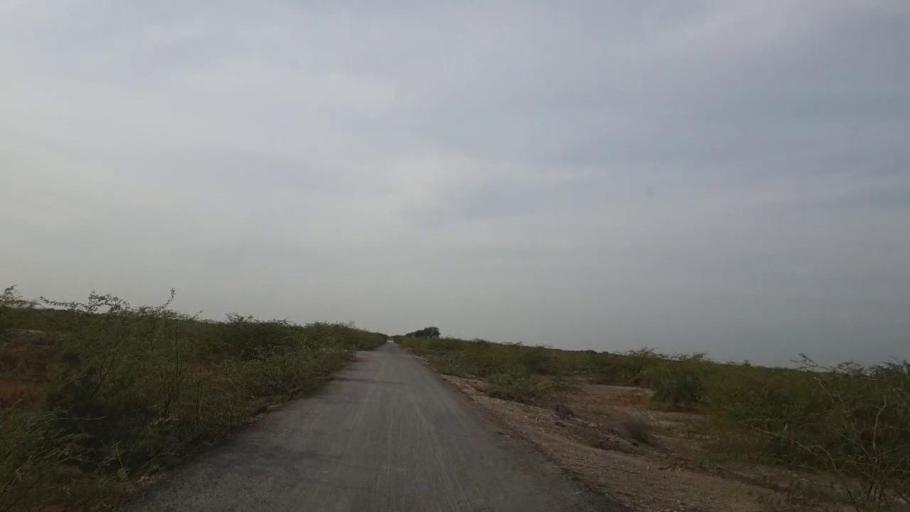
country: PK
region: Sindh
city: Nabisar
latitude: 24.9951
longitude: 69.5480
